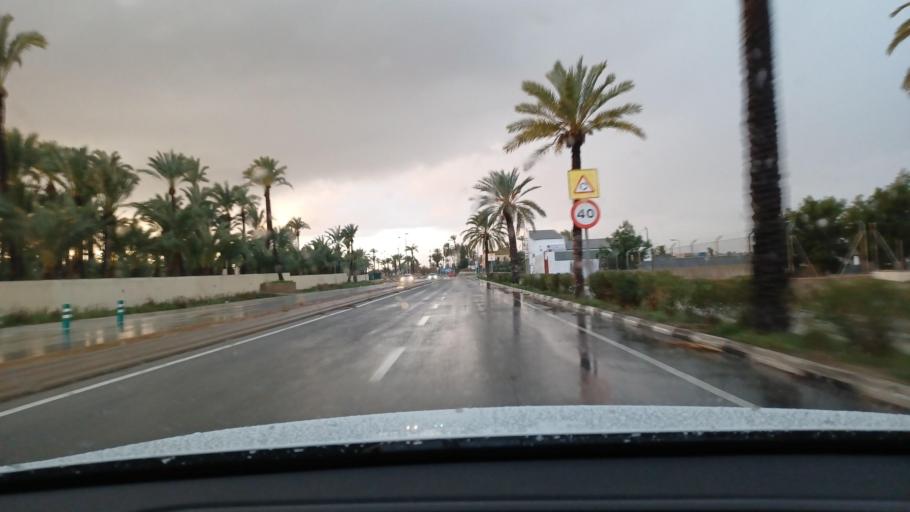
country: ES
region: Valencia
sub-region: Provincia de Alicante
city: Elche
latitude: 38.2451
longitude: -0.6989
